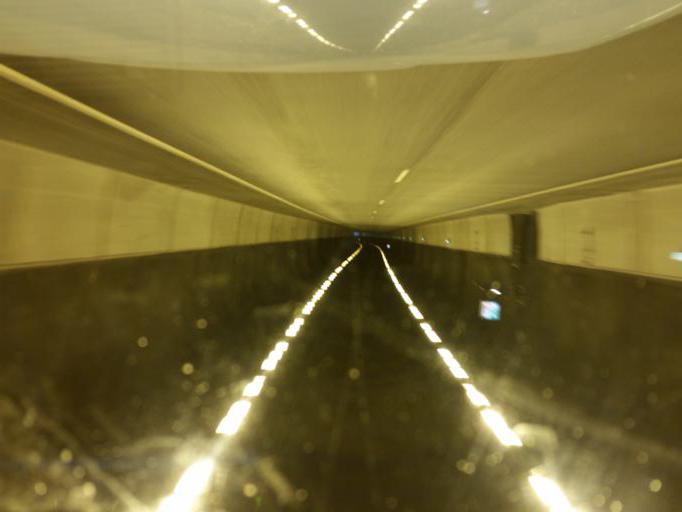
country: FI
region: Uusimaa
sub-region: Helsinki
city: Saukkola
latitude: 60.3246
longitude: 23.9532
